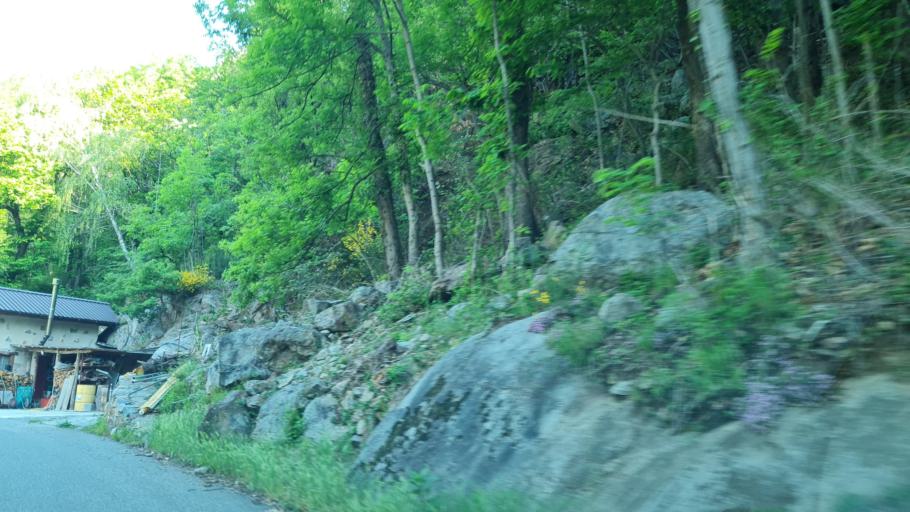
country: IT
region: Aosta Valley
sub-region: Valle d'Aosta
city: Bard
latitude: 45.6140
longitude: 7.7545
